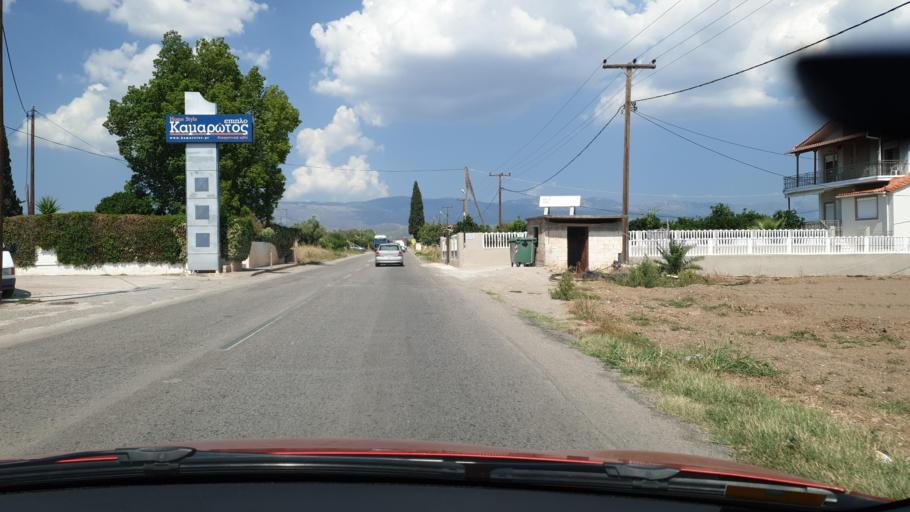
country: GR
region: Central Greece
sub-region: Nomos Evvoias
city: Kastella
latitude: 38.5478
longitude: 23.6292
